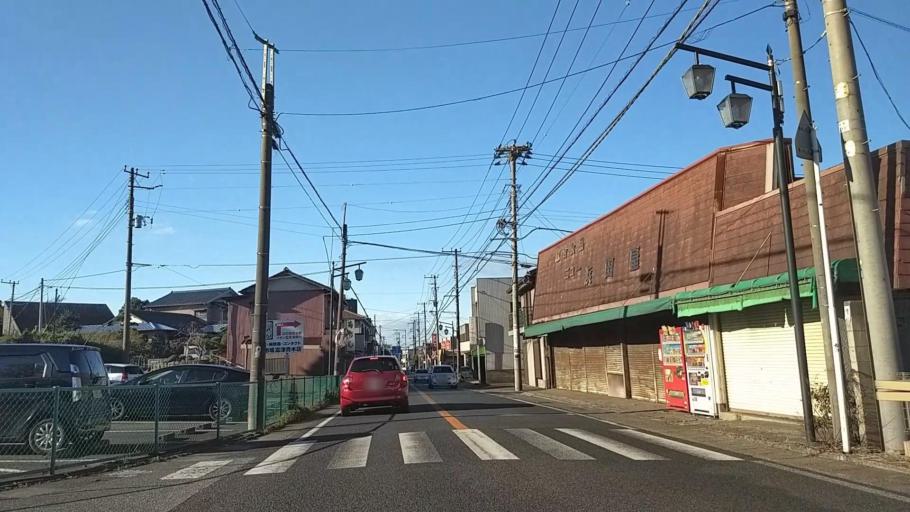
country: JP
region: Chiba
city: Kimitsu
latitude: 35.3312
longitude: 139.8577
